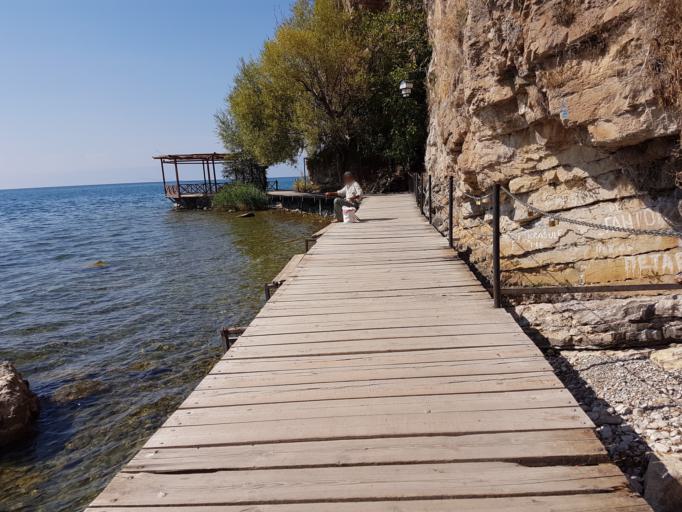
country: MK
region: Ohrid
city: Ohrid
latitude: 41.1111
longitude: 20.7928
